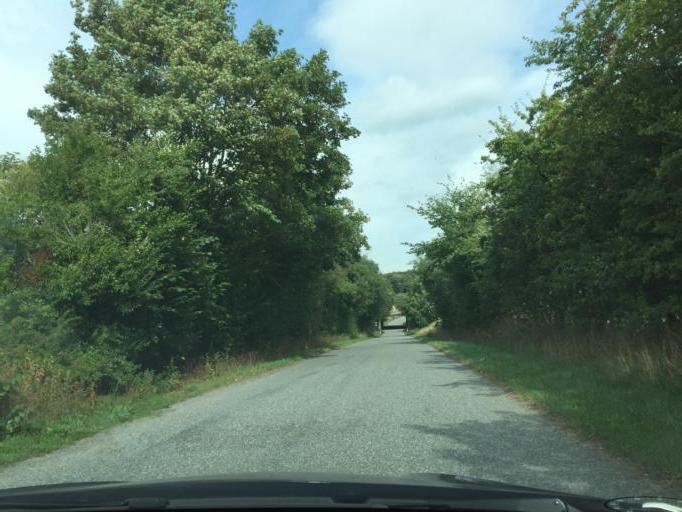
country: DK
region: South Denmark
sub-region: Assens Kommune
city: Vissenbjerg
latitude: 55.3971
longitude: 10.1656
